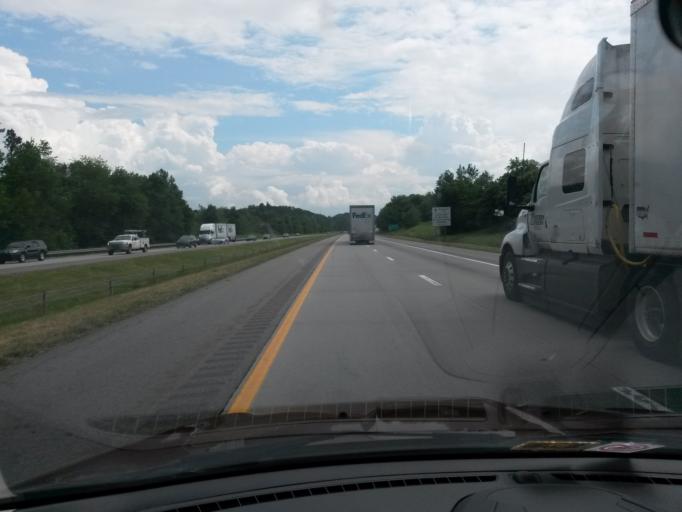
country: US
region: North Carolina
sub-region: Yadkin County
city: Jonesville
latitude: 36.1440
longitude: -80.8086
